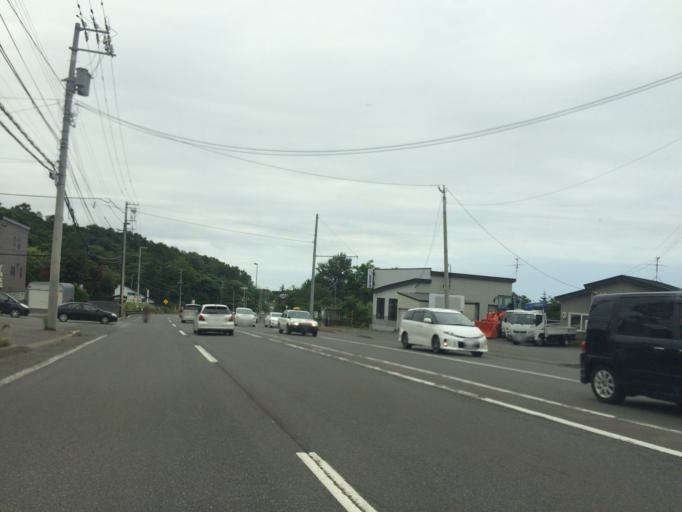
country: JP
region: Hokkaido
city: Otaru
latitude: 43.1492
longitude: 141.1348
